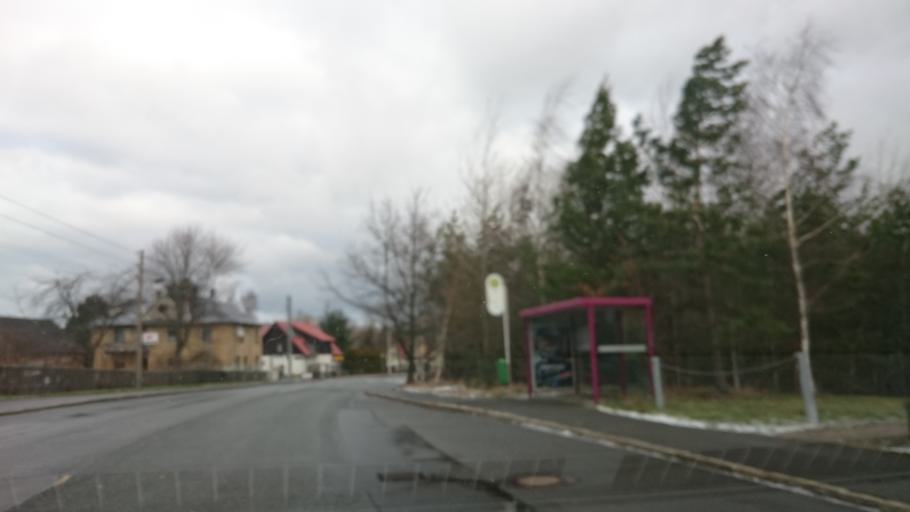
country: DE
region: Saxony
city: Hartmannsdorf
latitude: 50.7320
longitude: 12.4343
